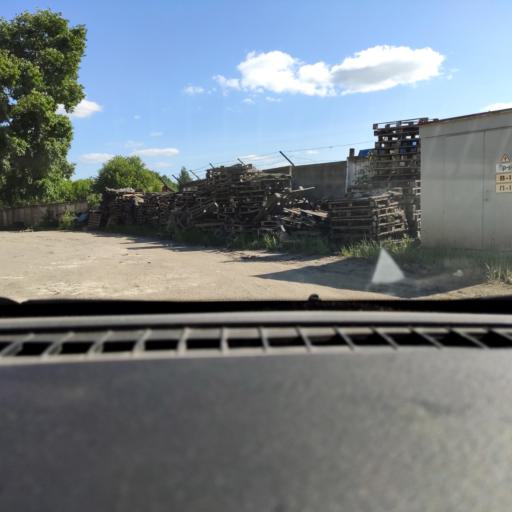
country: RU
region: Perm
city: Froly
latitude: 57.9518
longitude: 56.2543
